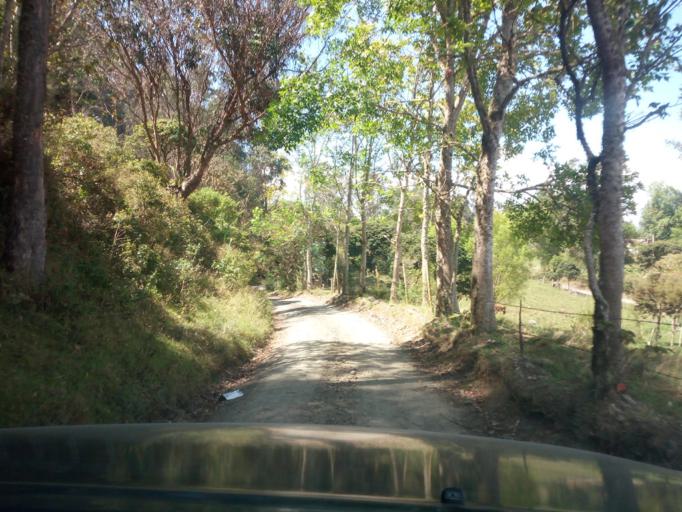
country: CO
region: Boyaca
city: Somondoco
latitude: 4.9713
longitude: -73.4076
